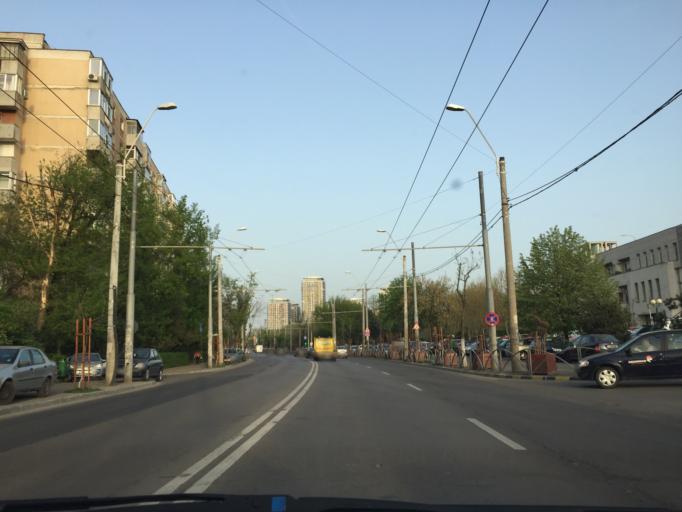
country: RO
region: Bucuresti
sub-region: Municipiul Bucuresti
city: Bucharest
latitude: 44.4086
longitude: 26.1145
